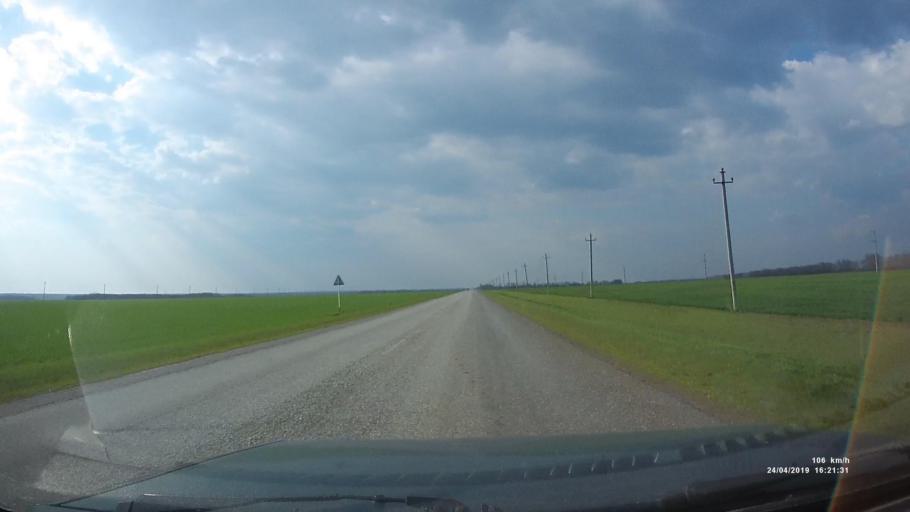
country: RU
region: Rostov
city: Orlovskiy
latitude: 46.8061
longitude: 42.0645
